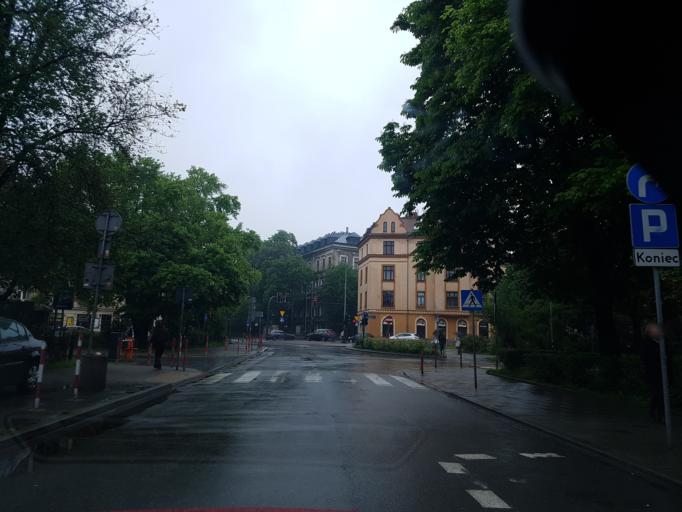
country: PL
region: Lesser Poland Voivodeship
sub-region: Krakow
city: Krakow
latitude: 50.0581
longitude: 19.9500
